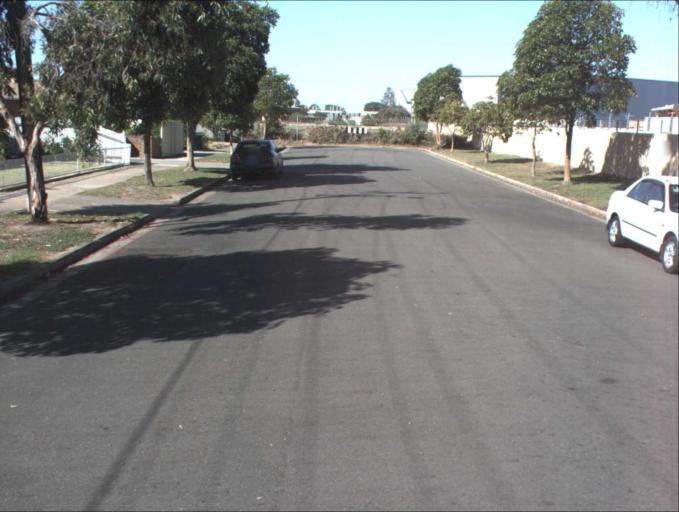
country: AU
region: South Australia
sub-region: Port Adelaide Enfield
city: Alberton
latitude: -34.8464
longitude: 138.5400
